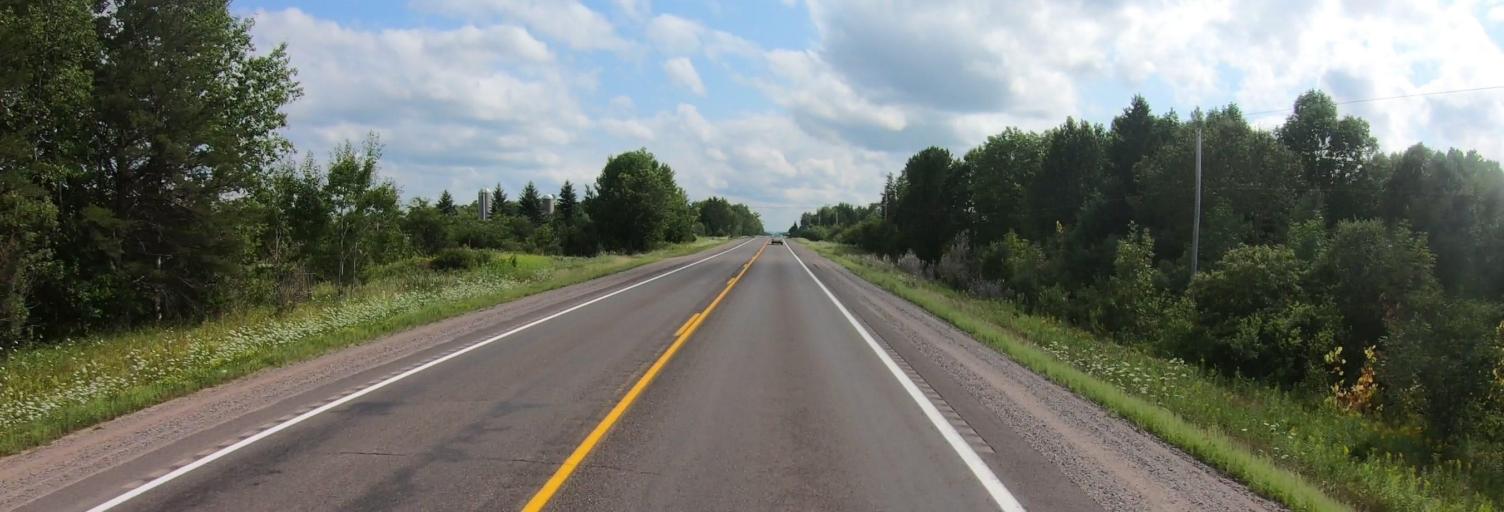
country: US
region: Michigan
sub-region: Ontonagon County
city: Ontonagon
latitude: 46.5820
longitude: -89.1785
